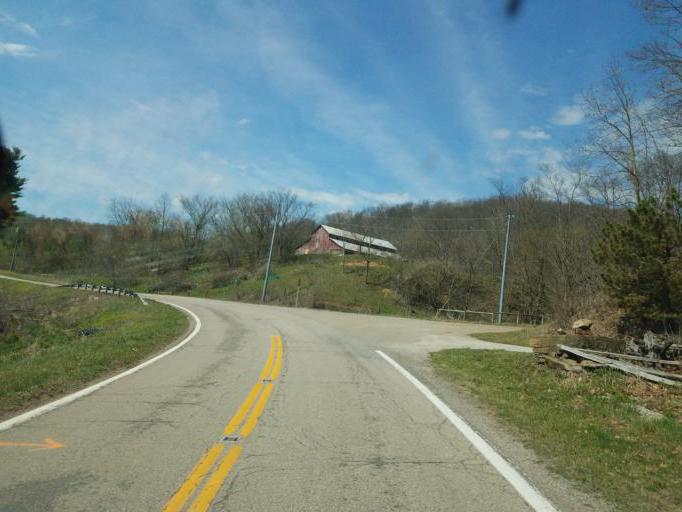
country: US
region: Ohio
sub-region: Knox County
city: Oak Hill
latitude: 40.3862
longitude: -82.2338
